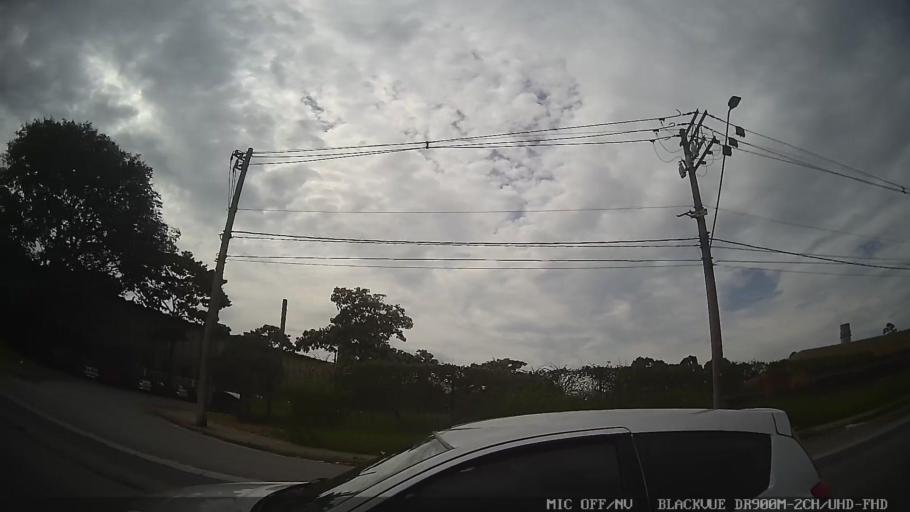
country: BR
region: Sao Paulo
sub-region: Maua
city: Maua
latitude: -23.6567
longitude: -46.4961
